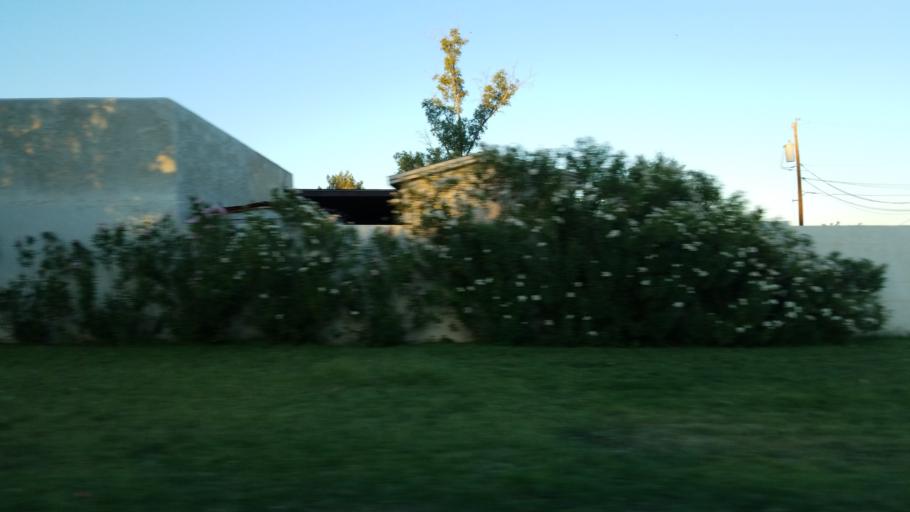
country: US
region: Arizona
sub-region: Maricopa County
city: Glendale
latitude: 33.5294
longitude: -112.1342
